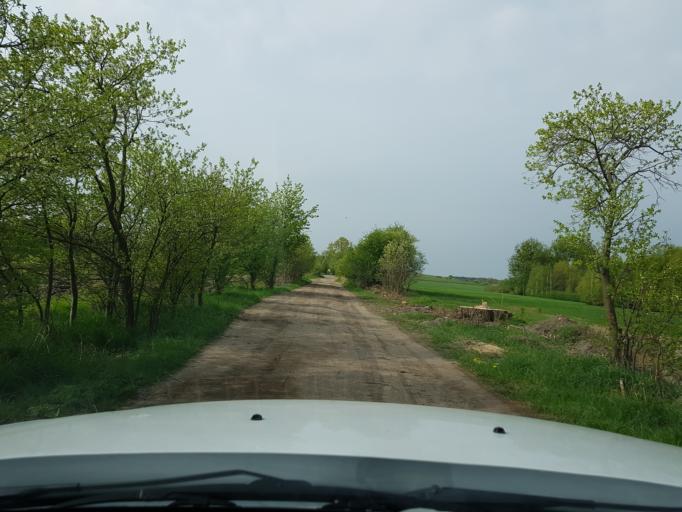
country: PL
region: West Pomeranian Voivodeship
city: Trzcinsko Zdroj
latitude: 52.9537
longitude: 14.5807
